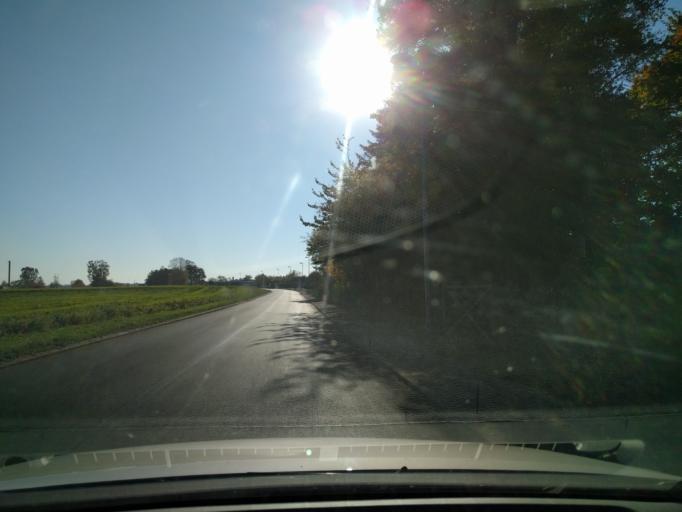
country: DK
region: Zealand
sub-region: Guldborgsund Kommune
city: Nykobing Falster
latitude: 54.8105
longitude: 11.8741
